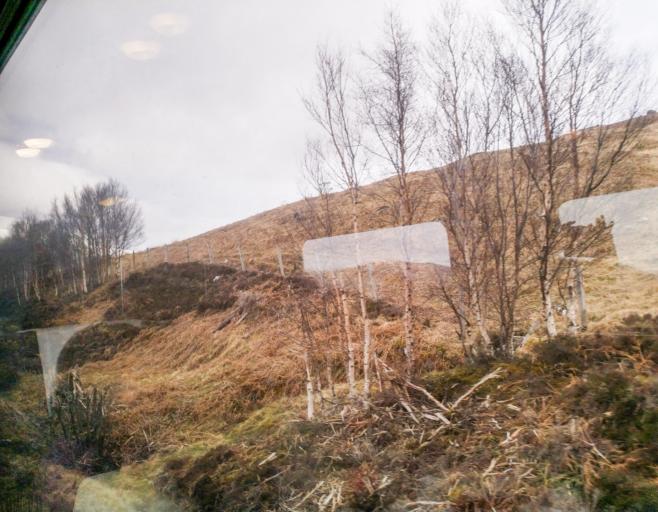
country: GB
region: Scotland
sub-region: Highland
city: Spean Bridge
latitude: 56.7788
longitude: -4.7324
